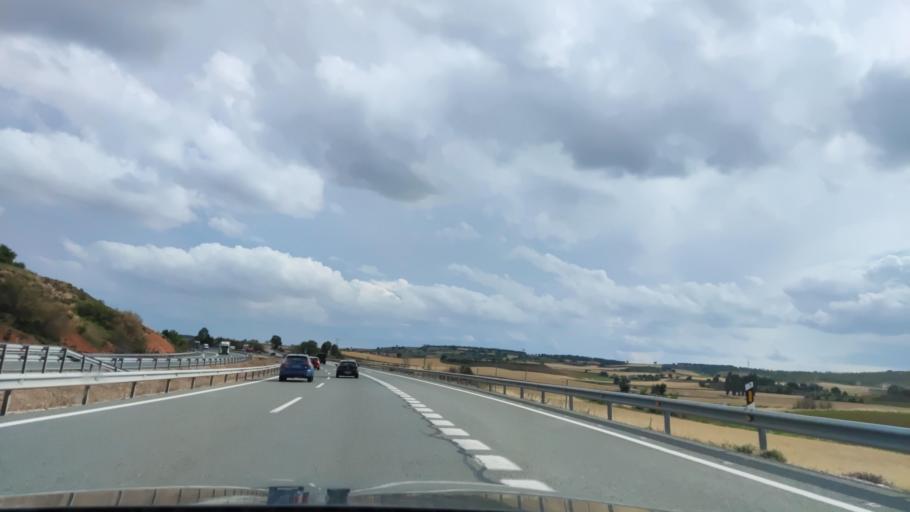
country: ES
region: Castille-La Mancha
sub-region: Provincia de Cuenca
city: Castillo de Garcimunoz
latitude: 39.6908
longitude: -2.3927
